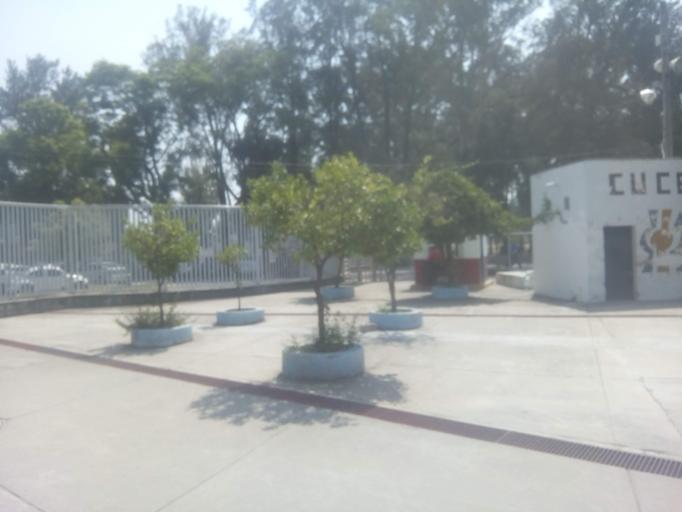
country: MX
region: Jalisco
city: Tlaquepaque
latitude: 20.6565
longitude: -103.3243
